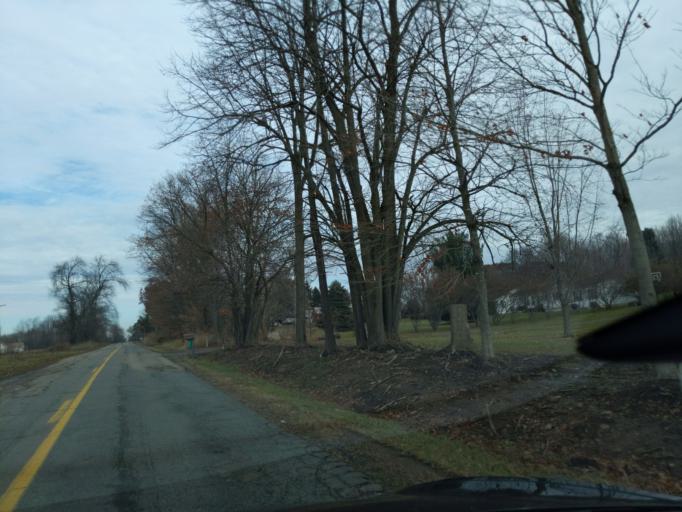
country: US
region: Michigan
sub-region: Ingham County
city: Leslie
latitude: 42.4680
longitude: -84.5020
